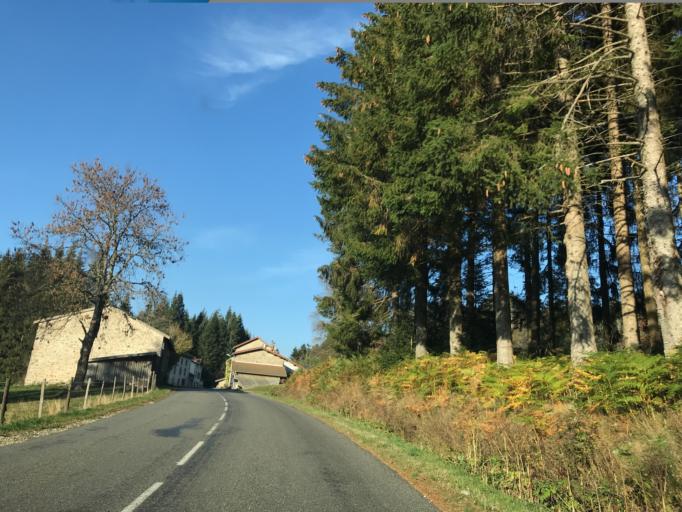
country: FR
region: Rhone-Alpes
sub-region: Departement de la Loire
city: Noiretable
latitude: 45.8011
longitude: 3.7143
